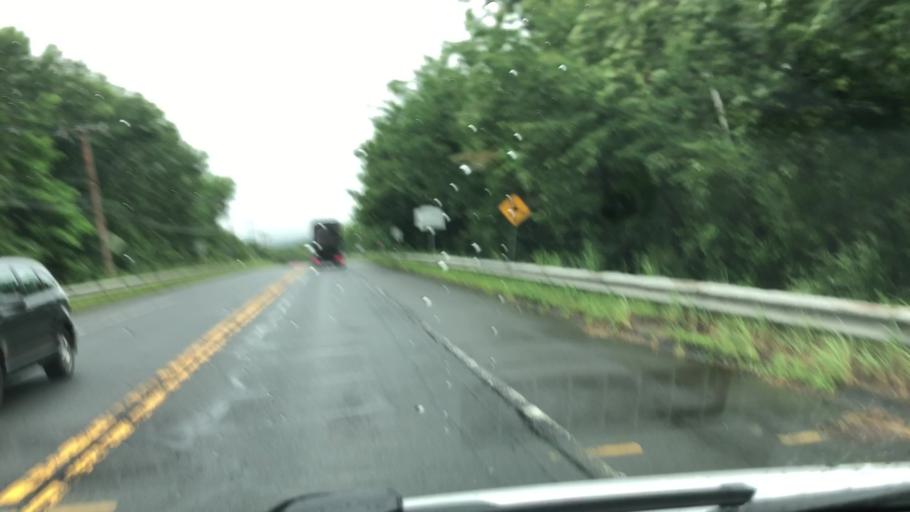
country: US
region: Massachusetts
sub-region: Franklin County
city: South Deerfield
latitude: 42.4684
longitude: -72.6099
